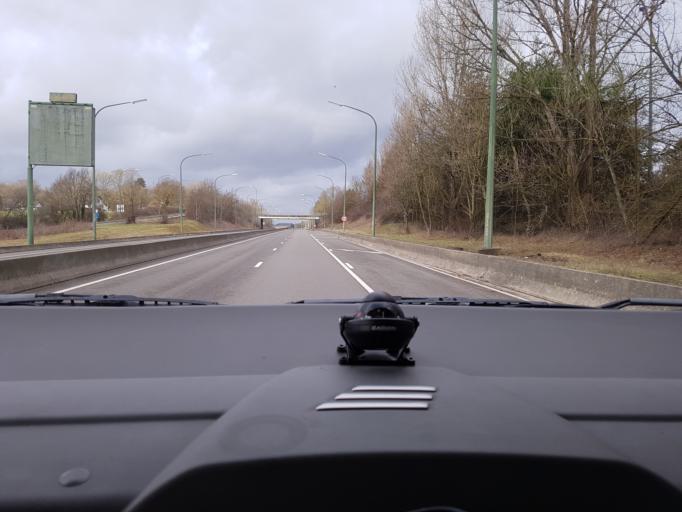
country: BE
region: Wallonia
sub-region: Province du Luxembourg
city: Marche-en-Famenne
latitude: 50.2264
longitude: 5.3353
